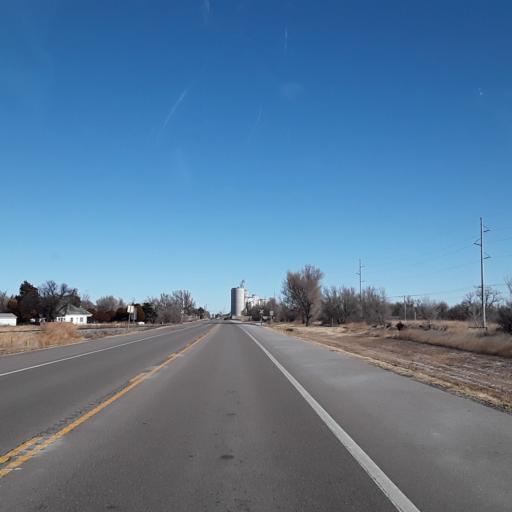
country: US
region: Kansas
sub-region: Pawnee County
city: Larned
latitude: 38.1692
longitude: -99.1083
